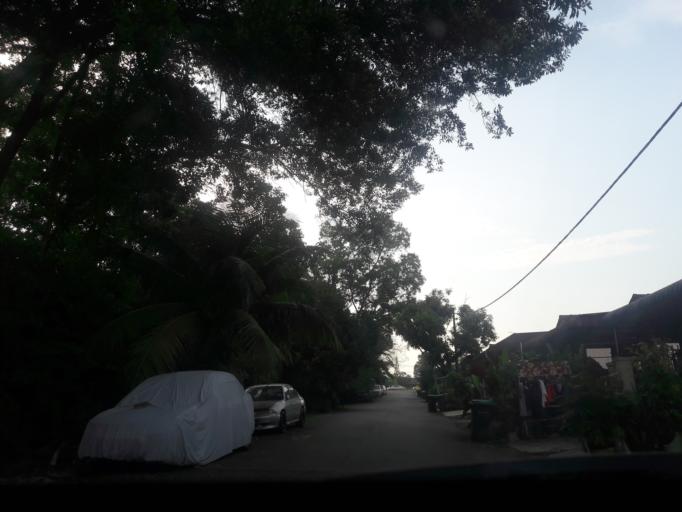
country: MY
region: Kedah
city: Kulim
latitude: 5.3732
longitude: 100.5334
